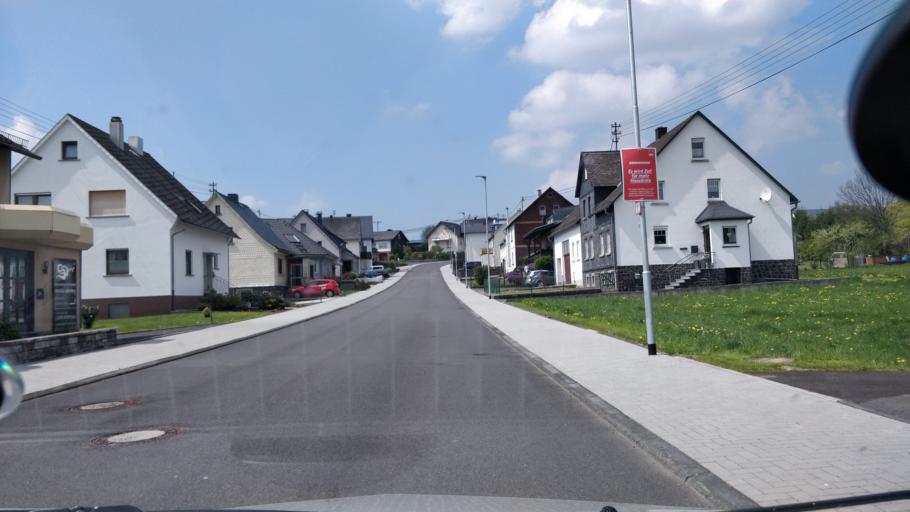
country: DE
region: Rheinland-Pfalz
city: Fehl-Ritzhausen
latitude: 50.6435
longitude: 8.0065
